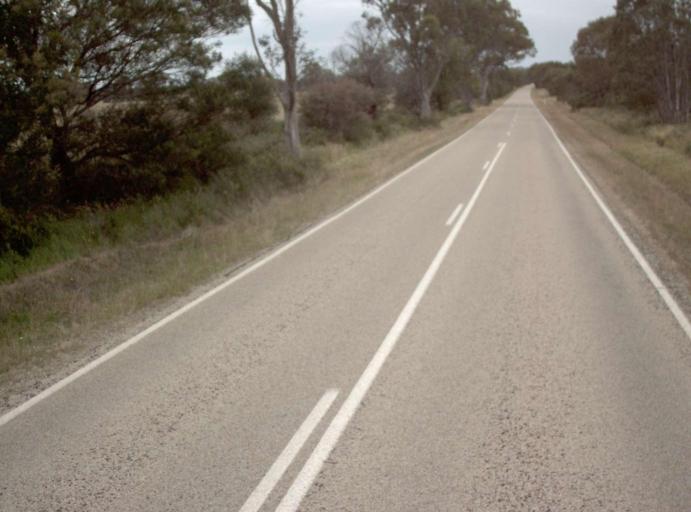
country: AU
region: Victoria
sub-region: East Gippsland
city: Bairnsdale
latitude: -37.9122
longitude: 147.5505
